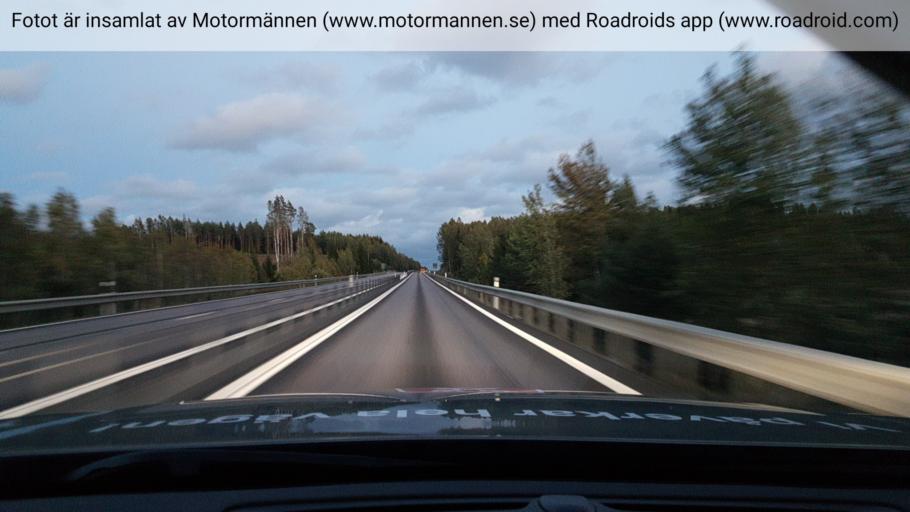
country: SE
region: Vaermland
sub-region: Karlstads Kommun
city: Skattkarr
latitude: 59.4012
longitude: 13.7888
